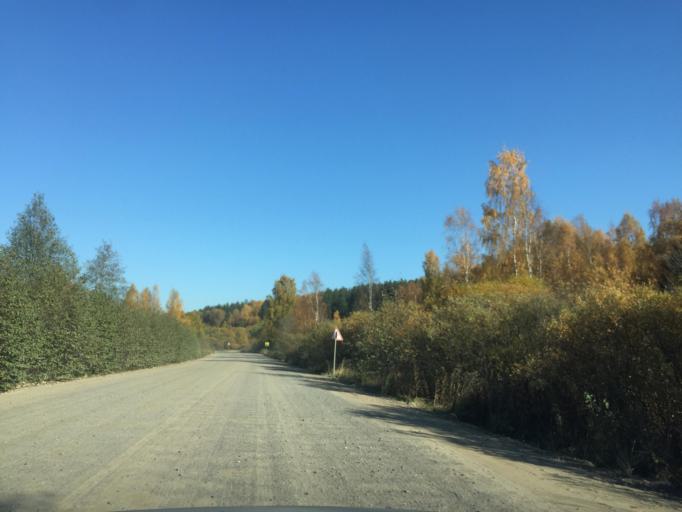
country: RU
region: Leningrad
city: Kuznechnoye
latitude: 61.3109
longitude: 29.9394
